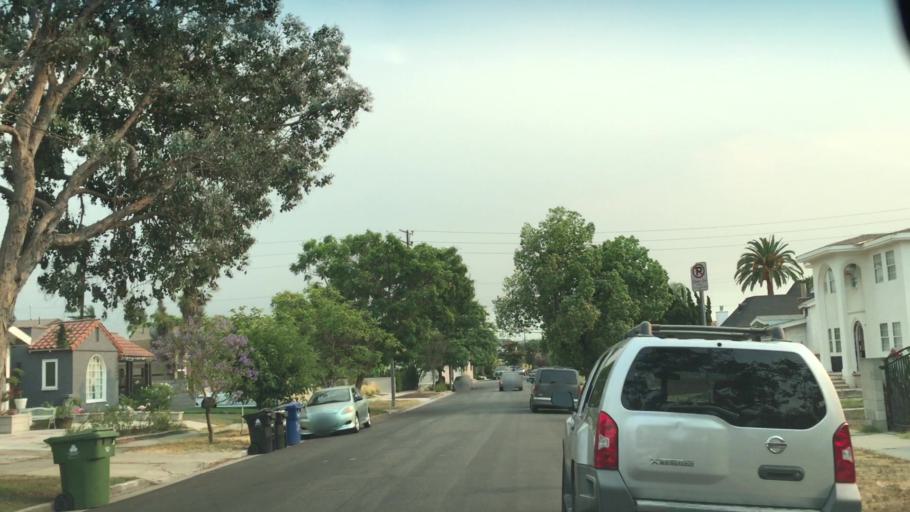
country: US
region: California
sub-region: Los Angeles County
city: Culver City
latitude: 34.0460
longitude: -118.3649
